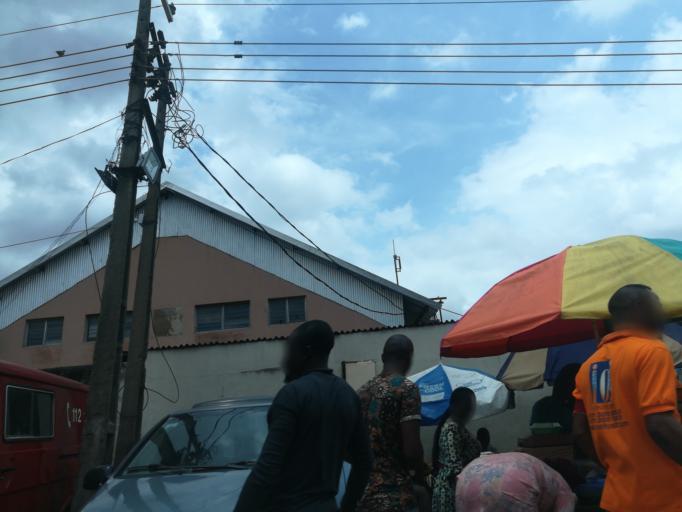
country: NG
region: Lagos
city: Oshodi
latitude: 6.5536
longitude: 3.3566
